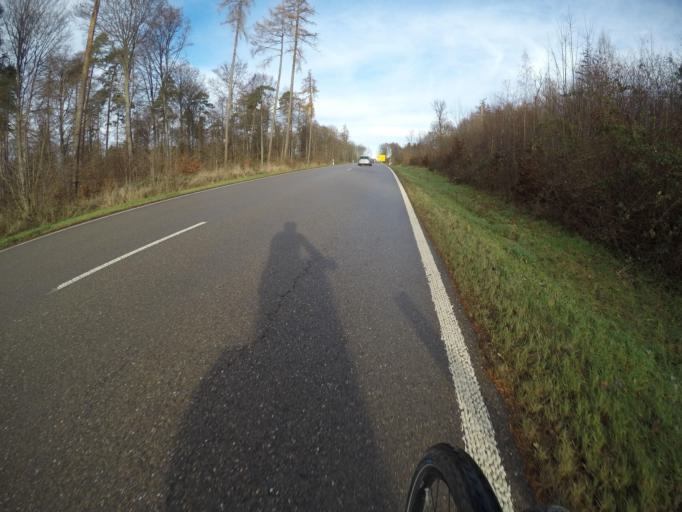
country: DE
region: Baden-Wuerttemberg
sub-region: Regierungsbezirk Stuttgart
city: Winterbach
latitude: 48.7738
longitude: 9.4591
